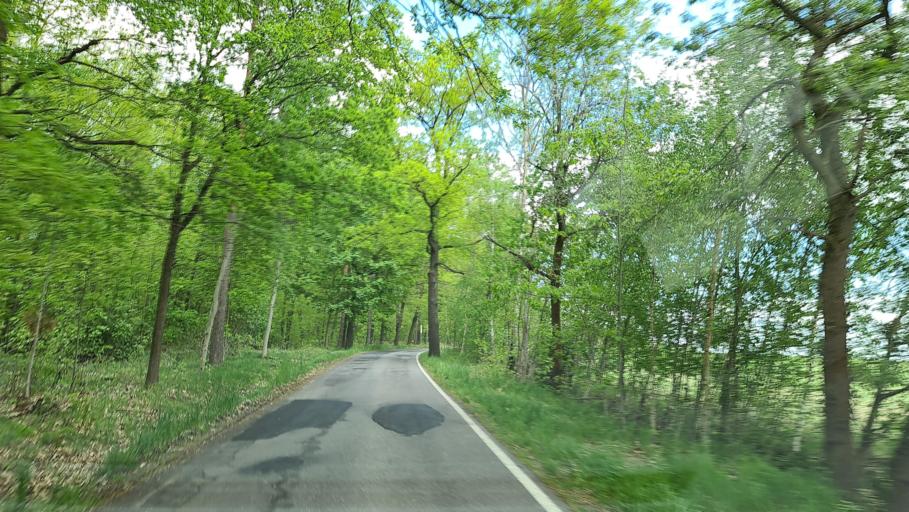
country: DE
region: Saxony
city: Hilbersdorf
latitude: 50.8430
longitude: 12.9869
